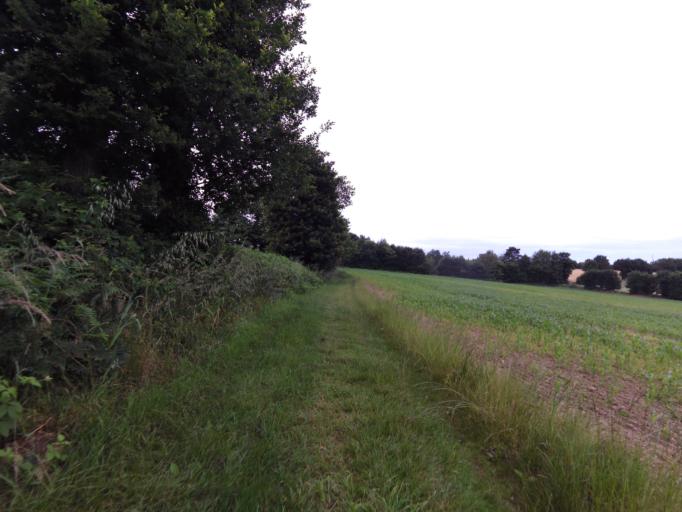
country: FR
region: Brittany
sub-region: Departement d'Ille-et-Vilaine
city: Chanteloup
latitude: 47.9303
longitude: -1.5971
